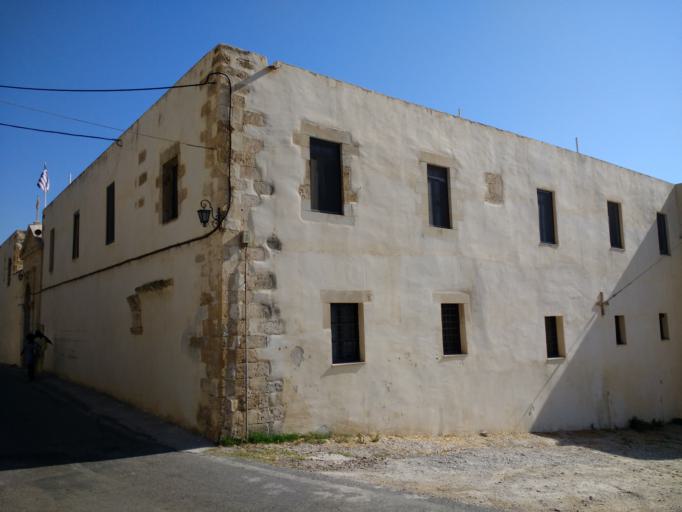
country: GR
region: Crete
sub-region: Nomos Chanias
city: Kolympari
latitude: 35.5503
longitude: 23.7767
